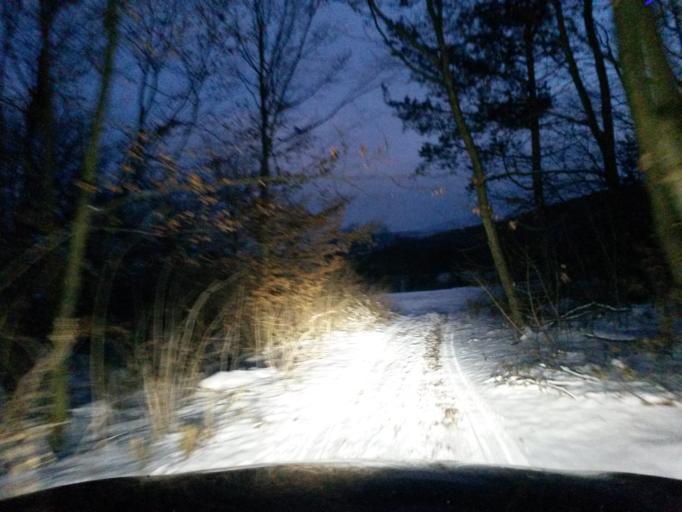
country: SK
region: Kosicky
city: Kosice
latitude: 48.7417
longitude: 21.3164
